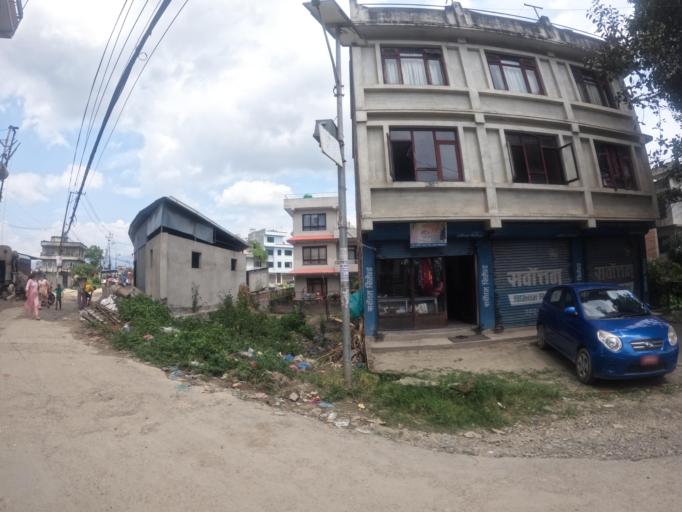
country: NP
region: Central Region
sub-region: Bagmati Zone
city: Bhaktapur
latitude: 27.6868
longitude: 85.3827
